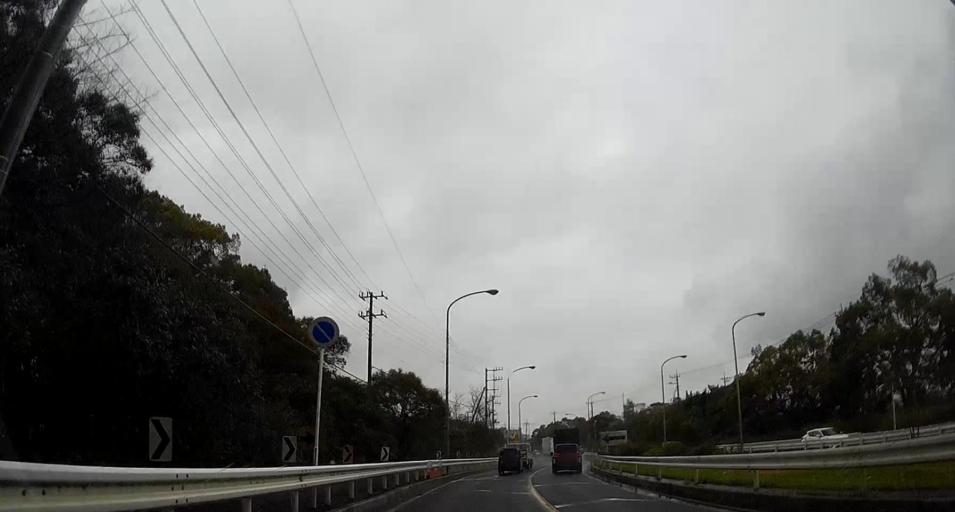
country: JP
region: Chiba
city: Ichihara
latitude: 35.5286
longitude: 140.0961
